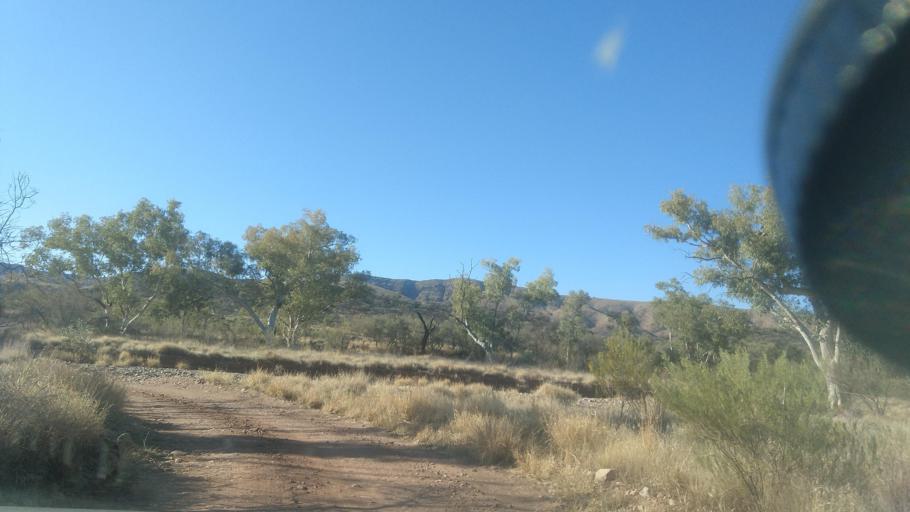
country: AU
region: Northern Territory
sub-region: Alice Springs
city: Alice Springs
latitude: -23.7529
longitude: 132.9184
